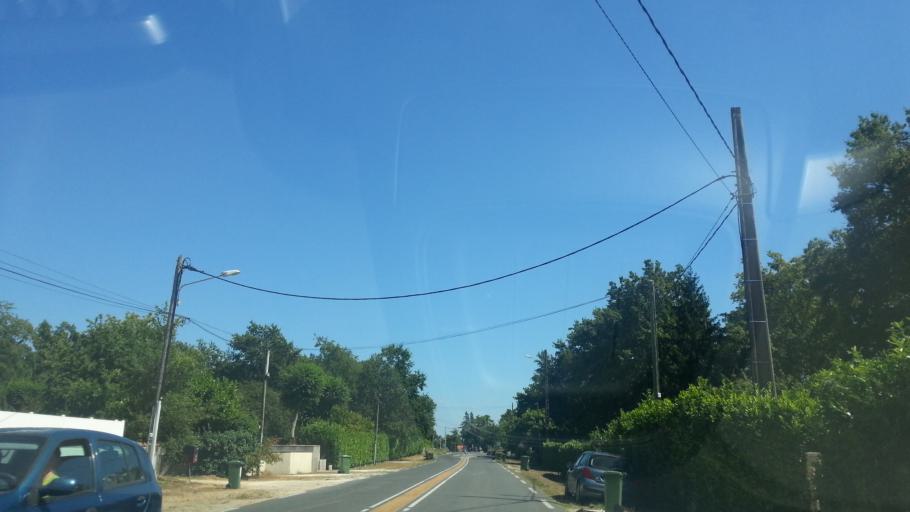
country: FR
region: Aquitaine
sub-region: Departement de la Gironde
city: Illats
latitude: 44.5614
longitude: -0.3633
